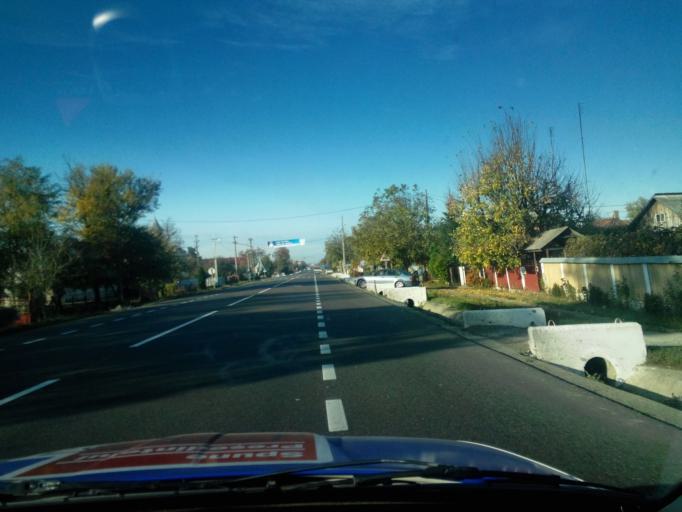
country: RO
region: Bacau
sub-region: Comuna Filipesti
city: Filipesti
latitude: 46.7384
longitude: 26.8860
